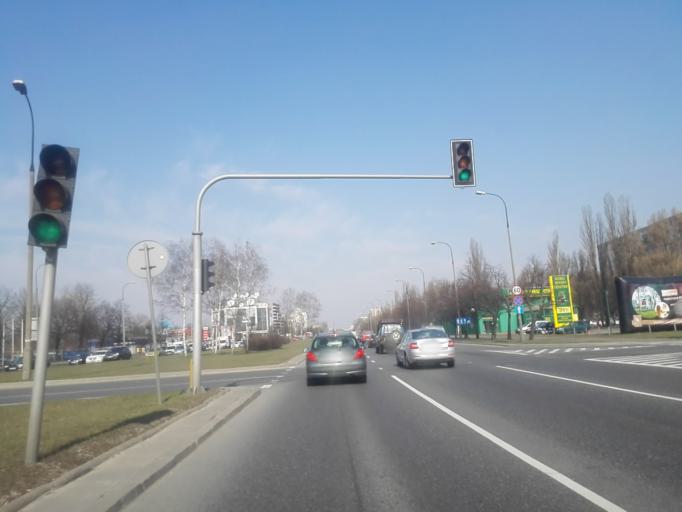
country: PL
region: Masovian Voivodeship
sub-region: Warszawa
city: Mokotow
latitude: 52.1771
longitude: 21.0446
